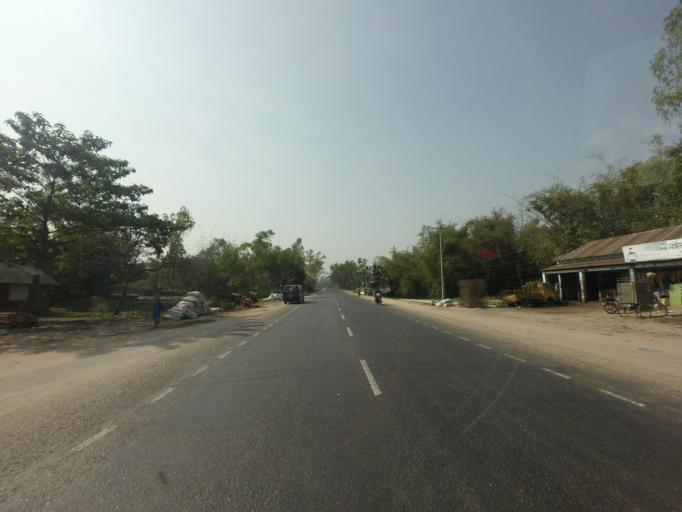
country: BD
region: Sylhet
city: Habiganj
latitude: 24.4172
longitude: 91.5663
